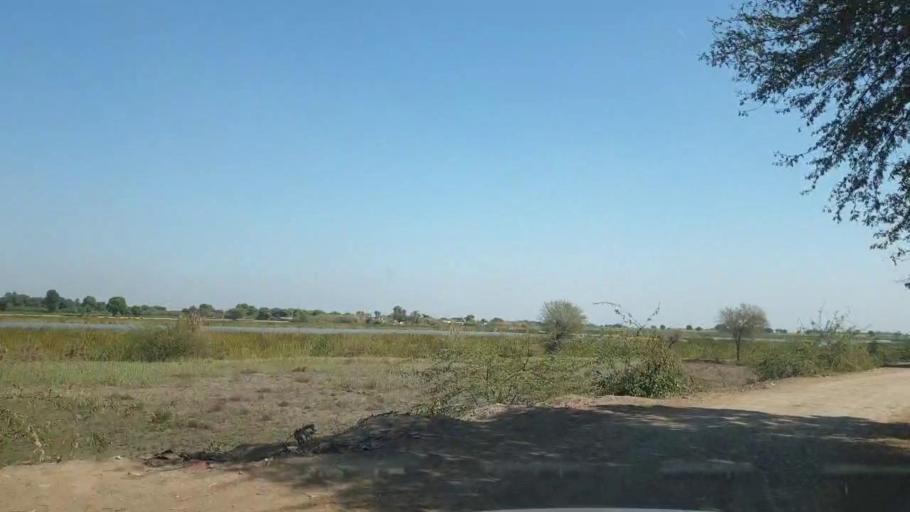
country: PK
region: Sindh
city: Tando Adam
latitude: 25.6409
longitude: 68.7071
